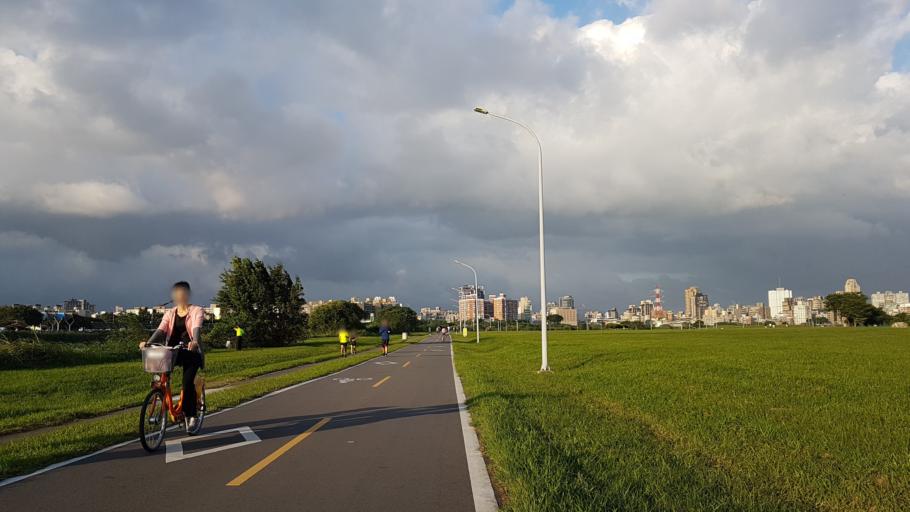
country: TW
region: Taipei
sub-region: Taipei
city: Banqiao
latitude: 25.0164
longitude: 121.5054
